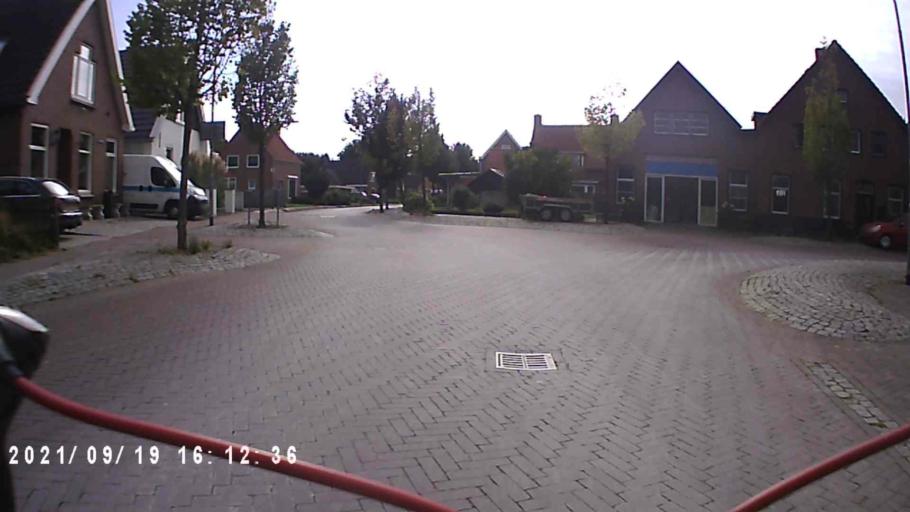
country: DE
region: Lower Saxony
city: Bunde
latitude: 53.1802
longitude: 7.2096
